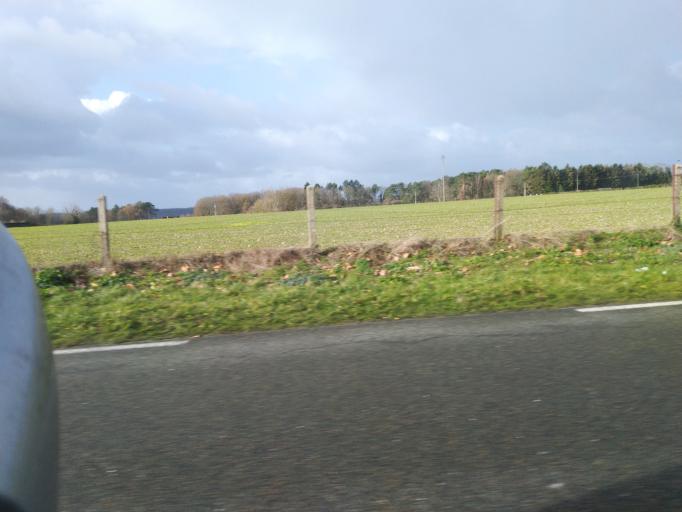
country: FR
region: Haute-Normandie
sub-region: Departement de la Seine-Maritime
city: Yainville
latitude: 49.4468
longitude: 0.8280
